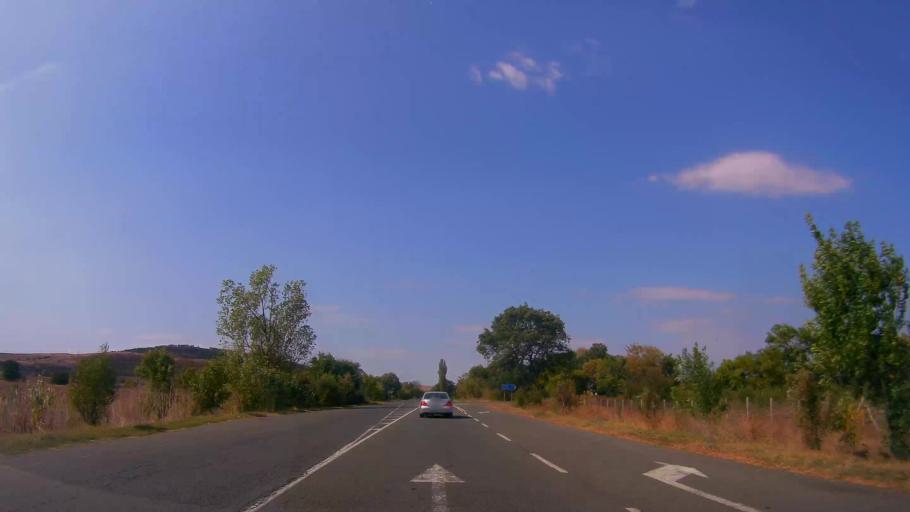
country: BG
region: Burgas
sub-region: Obshtina Karnobat
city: Karnobat
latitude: 42.6580
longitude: 27.0179
